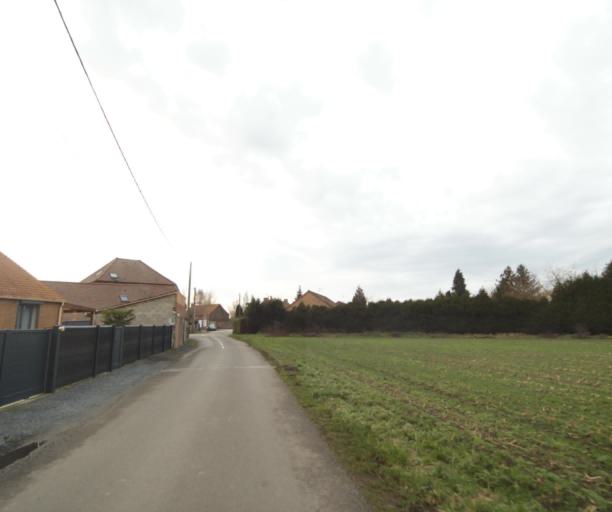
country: FR
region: Nord-Pas-de-Calais
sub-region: Departement du Nord
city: Hergnies
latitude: 50.4831
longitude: 3.5246
